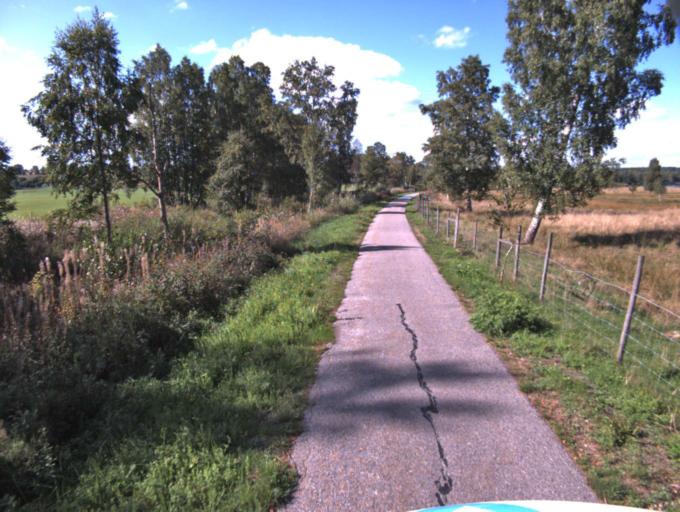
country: SE
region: Vaestra Goetaland
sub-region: Ulricehamns Kommun
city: Ulricehamn
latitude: 57.8385
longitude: 13.3070
